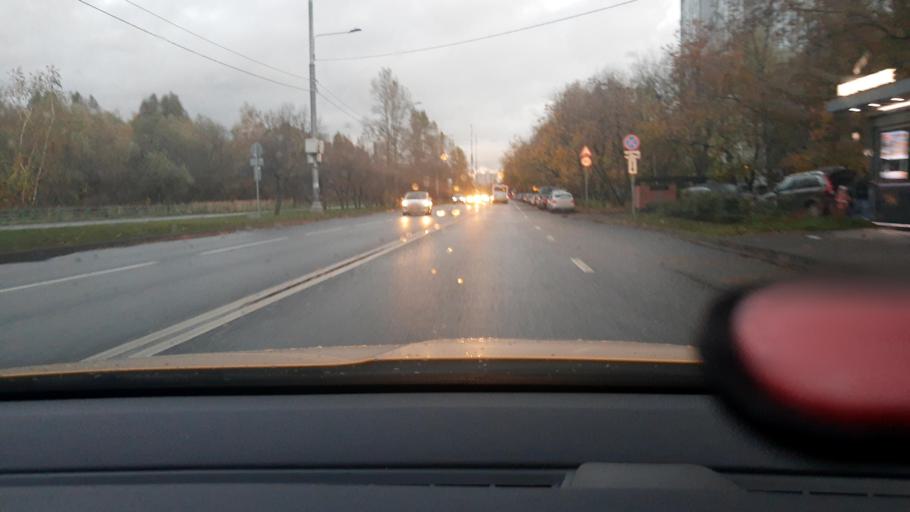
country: RU
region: Moscow
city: Strogino
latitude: 55.8153
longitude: 37.4069
